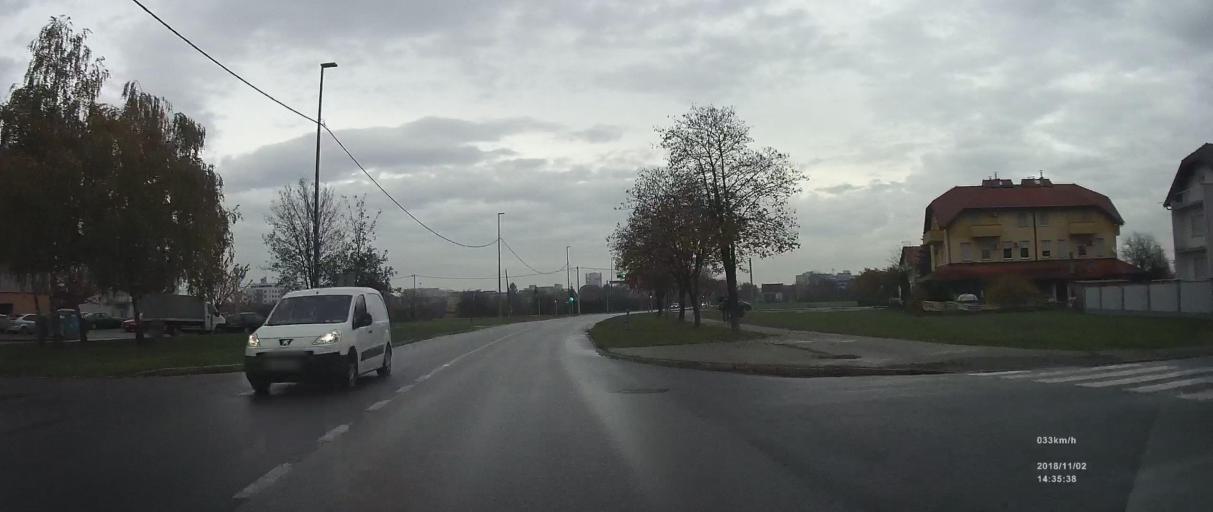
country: HR
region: Zagrebacka
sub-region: Grad Velika Gorica
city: Velika Gorica
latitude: 45.7047
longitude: 16.0636
